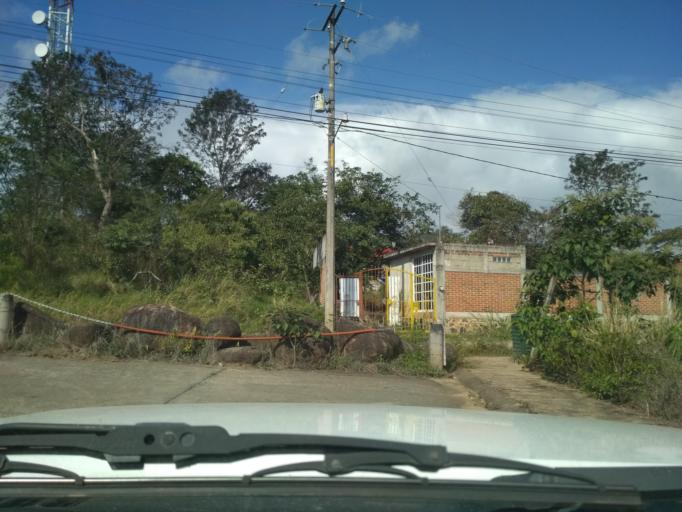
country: MX
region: Veracruz
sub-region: Emiliano Zapata
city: Jacarandas
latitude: 19.4987
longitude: -96.8417
